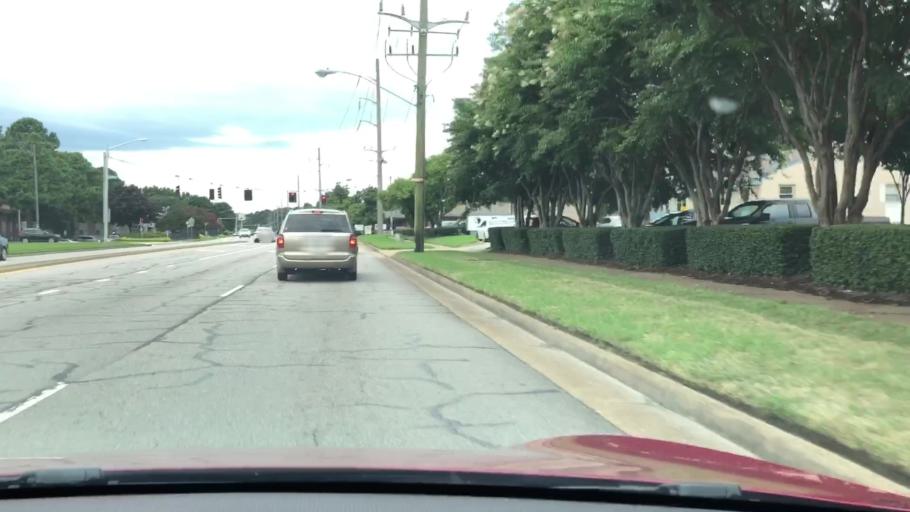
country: US
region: Virginia
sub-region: City of Virginia Beach
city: Virginia Beach
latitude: 36.8605
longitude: -76.0267
